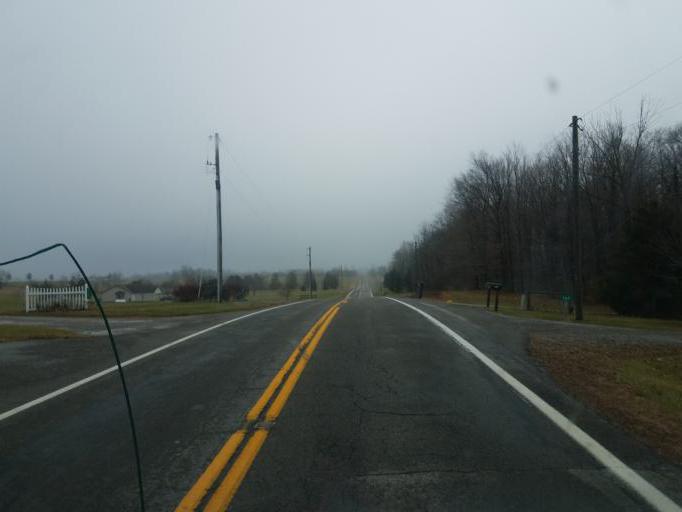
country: US
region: Ohio
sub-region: Champaign County
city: North Lewisburg
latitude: 40.2753
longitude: -83.5986
